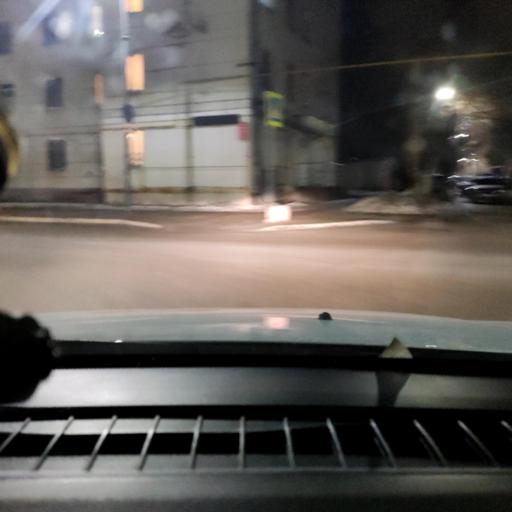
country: RU
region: Samara
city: Novokuybyshevsk
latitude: 53.0949
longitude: 49.9463
